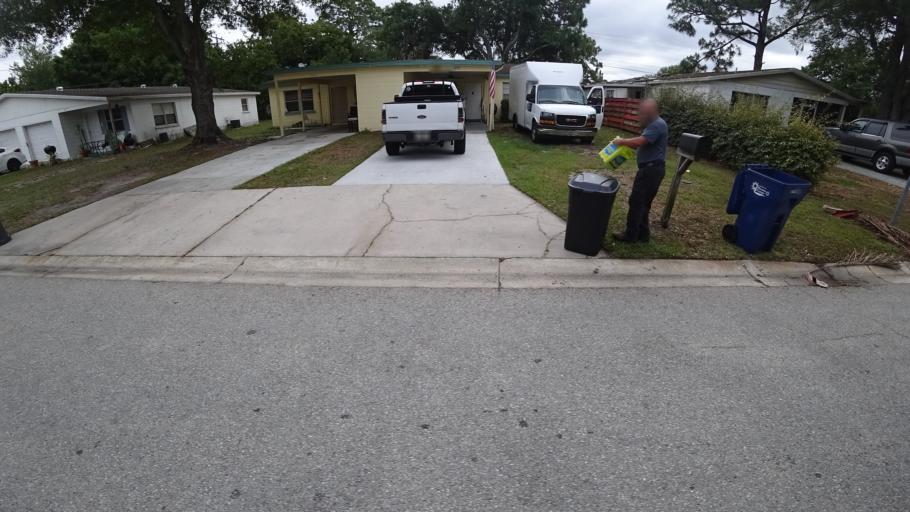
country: US
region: Florida
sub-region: Manatee County
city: South Bradenton
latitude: 27.4522
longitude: -82.5840
